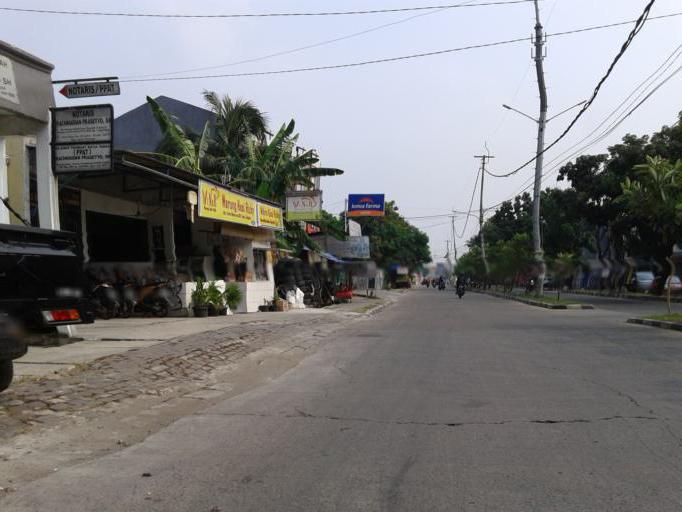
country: ID
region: West Java
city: Pamulang
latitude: -6.3505
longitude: 106.7763
